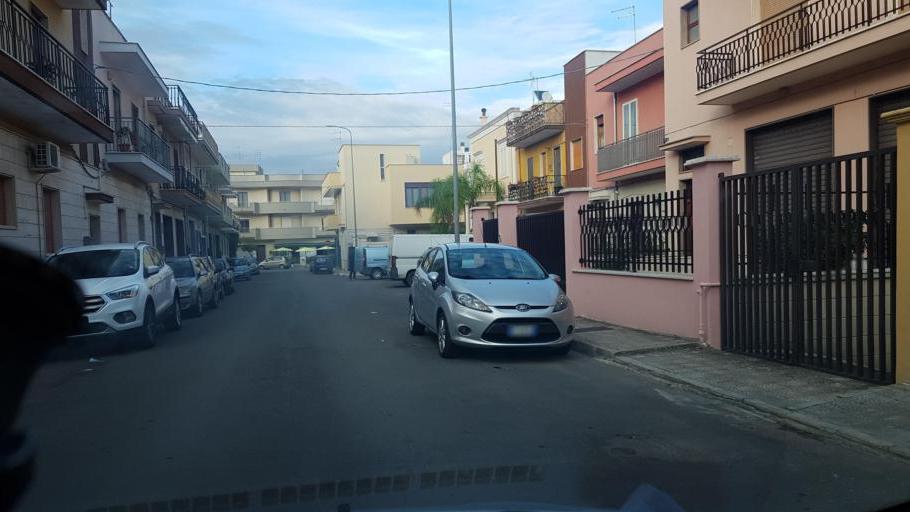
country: IT
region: Apulia
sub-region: Provincia di Brindisi
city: Francavilla Fontana
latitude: 40.5231
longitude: 17.5927
